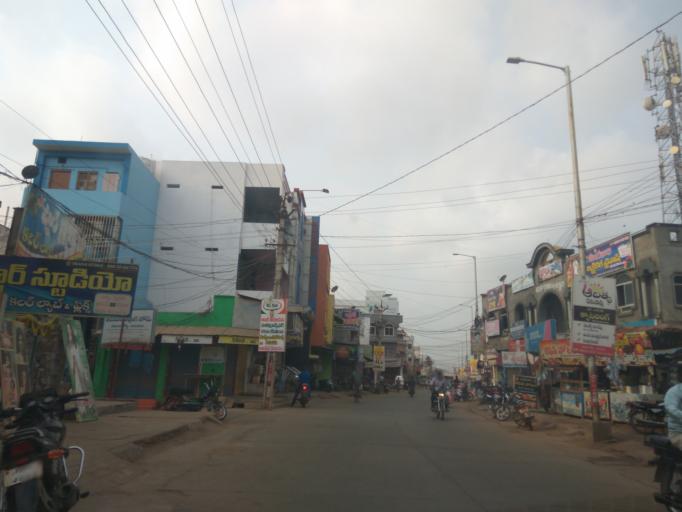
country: IN
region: Andhra Pradesh
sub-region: Prakasam
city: Kandukur
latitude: 15.2163
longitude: 79.9039
